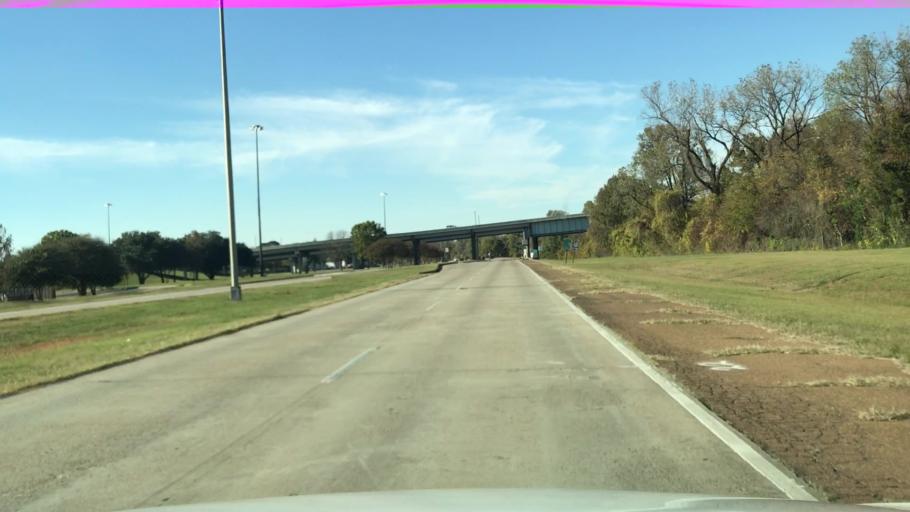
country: US
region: Louisiana
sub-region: Bossier Parish
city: Bossier City
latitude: 32.4890
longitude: -93.6987
